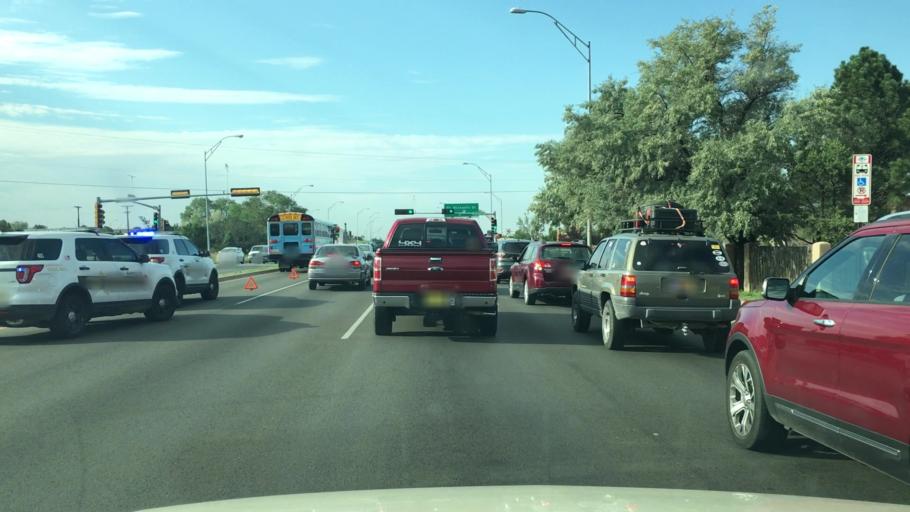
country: US
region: New Mexico
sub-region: Santa Fe County
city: Santa Fe
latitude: 35.6628
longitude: -105.9565
